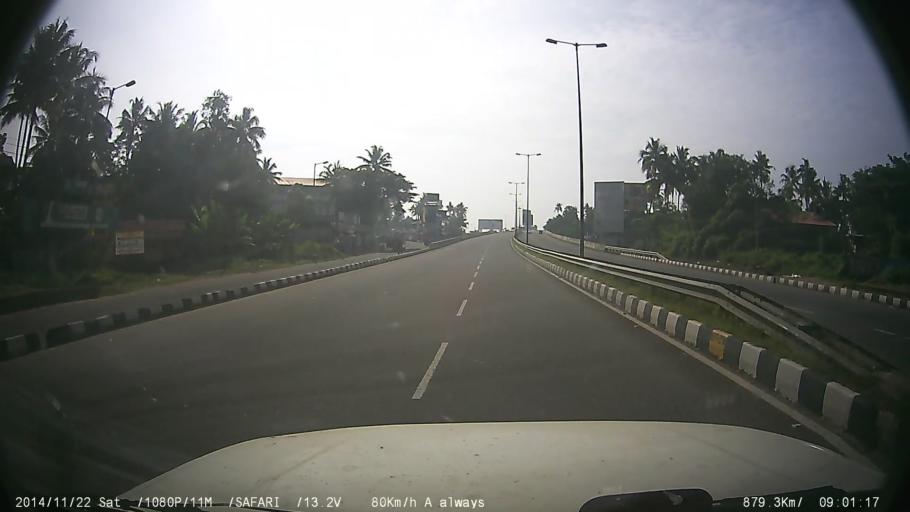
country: IN
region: Kerala
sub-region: Thrissur District
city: Kizhake Chalakudi
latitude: 10.3751
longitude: 76.3011
